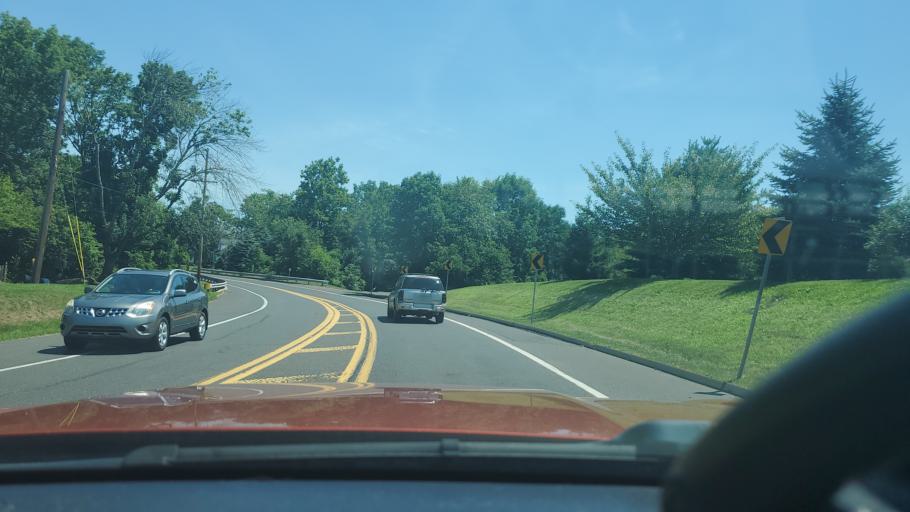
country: US
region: Pennsylvania
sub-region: Montgomery County
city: Limerick
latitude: 40.2282
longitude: -75.5321
